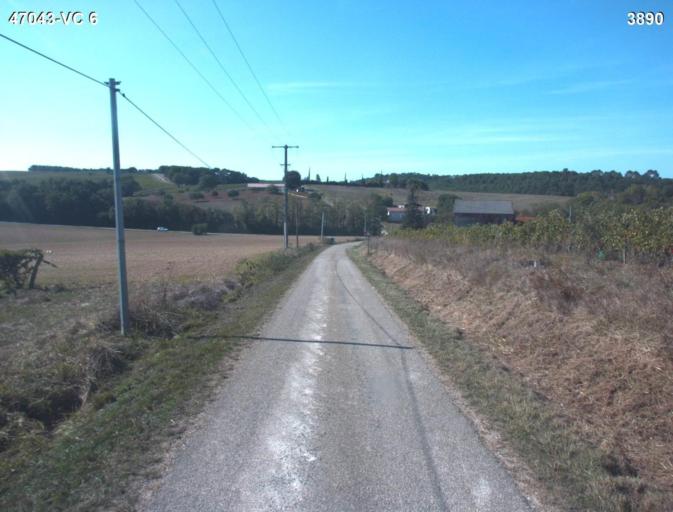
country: FR
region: Aquitaine
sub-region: Departement du Lot-et-Garonne
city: Buzet-sur-Baise
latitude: 44.2302
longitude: 0.2784
